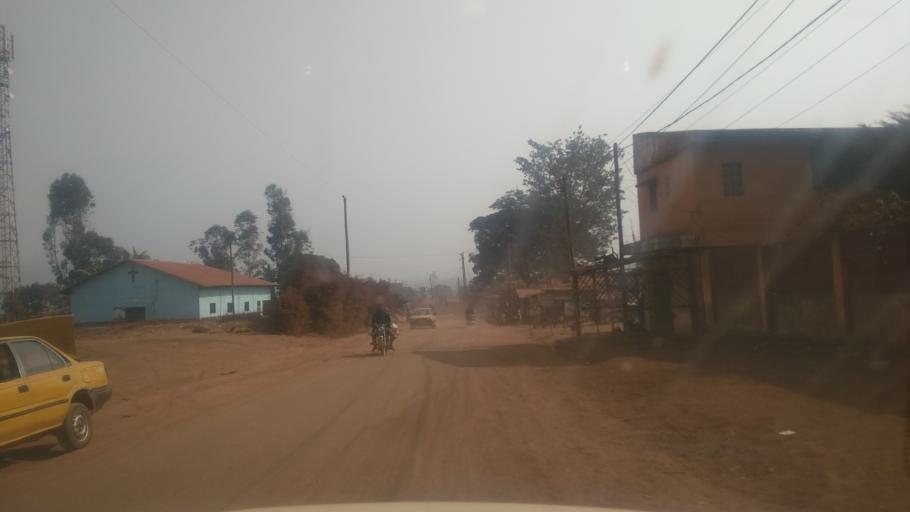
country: CM
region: West
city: Bafoussam
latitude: 5.5067
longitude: 10.4012
